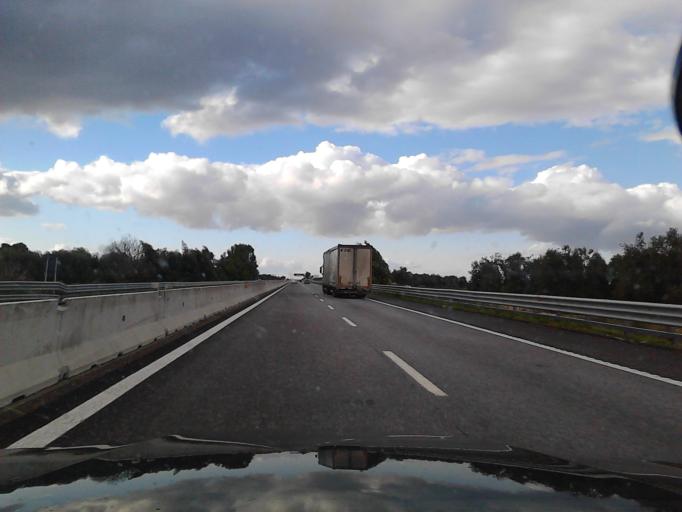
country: IT
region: Apulia
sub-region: Provincia di Barletta - Andria - Trani
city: Andria
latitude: 41.2505
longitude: 16.3235
